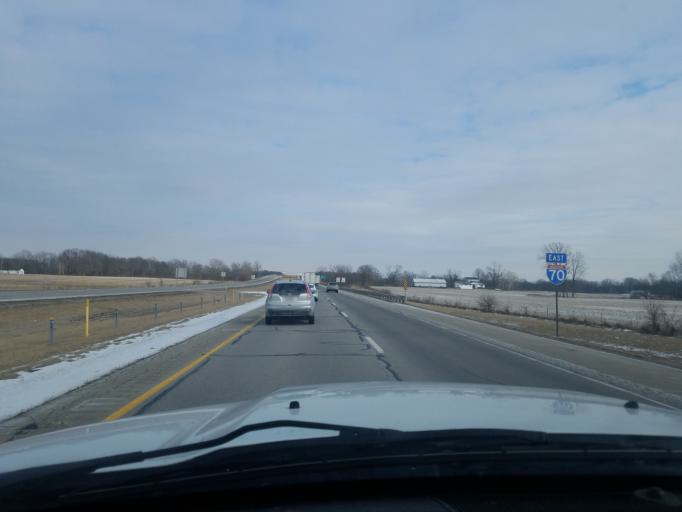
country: US
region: Indiana
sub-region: Wayne County
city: Cambridge City
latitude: 39.8519
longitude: -85.2532
